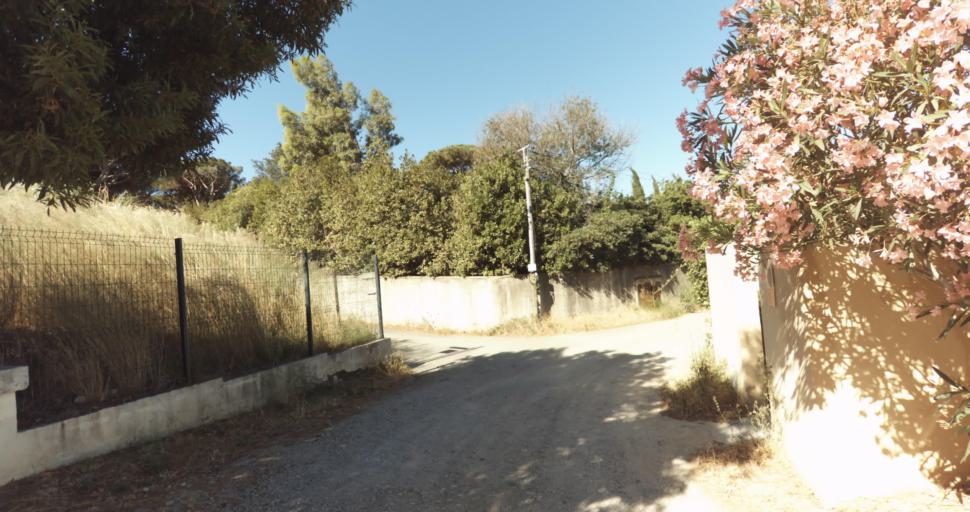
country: FR
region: Provence-Alpes-Cote d'Azur
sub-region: Departement du Var
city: Saint-Tropez
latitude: 43.2589
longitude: 6.6234
